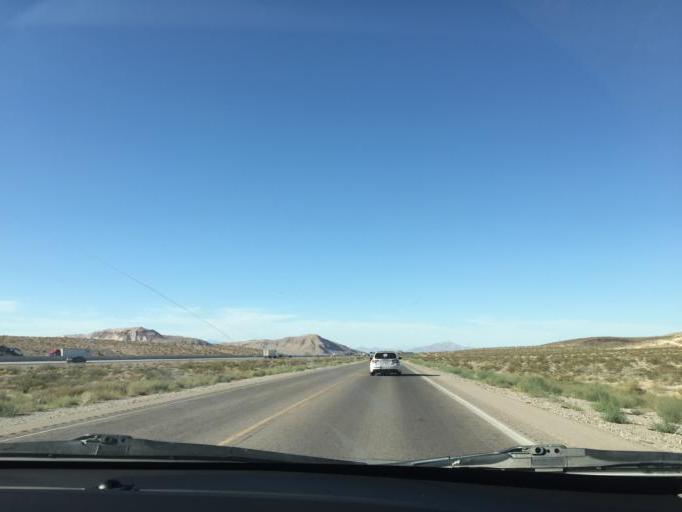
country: US
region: Nevada
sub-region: Clark County
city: Enterprise
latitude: 35.9014
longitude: -115.2124
